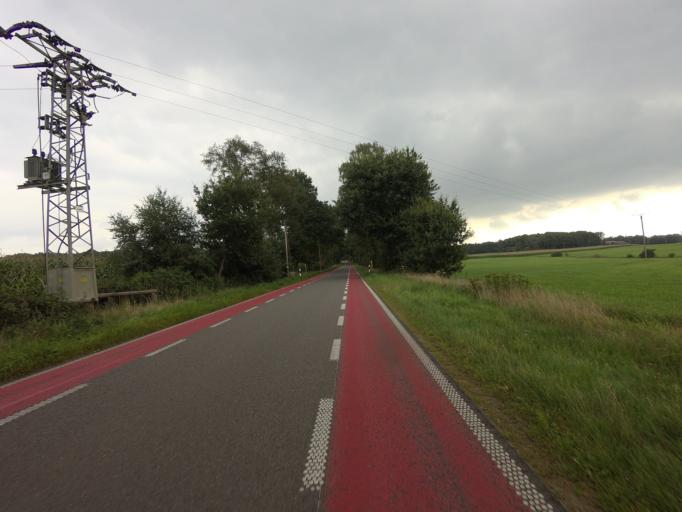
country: DE
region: Lower Saxony
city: Getelo
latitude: 52.4587
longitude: 6.8596
